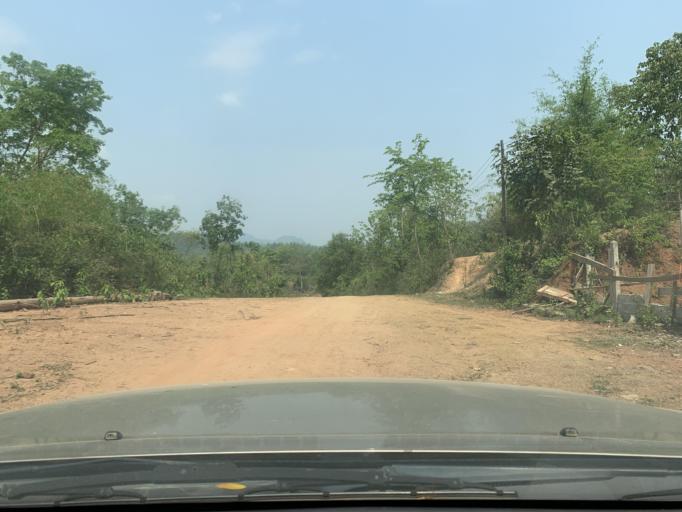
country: LA
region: Louangphabang
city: Louangphabang
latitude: 19.9369
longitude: 102.1484
